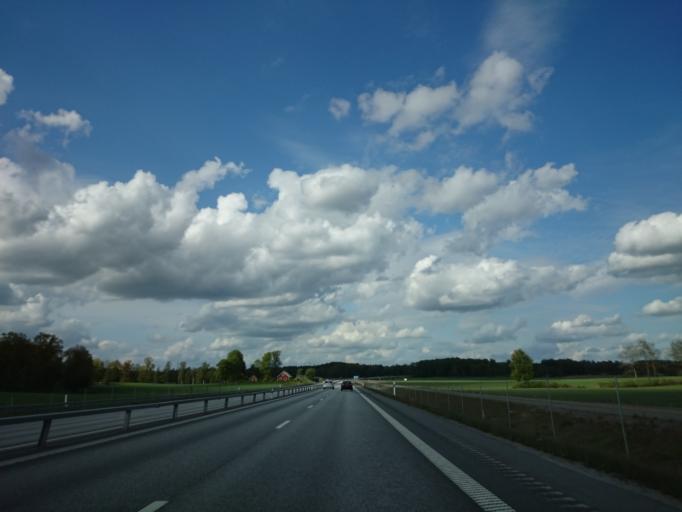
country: SE
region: Skane
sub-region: Horby Kommun
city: Hoerby
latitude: 55.8919
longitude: 13.7206
